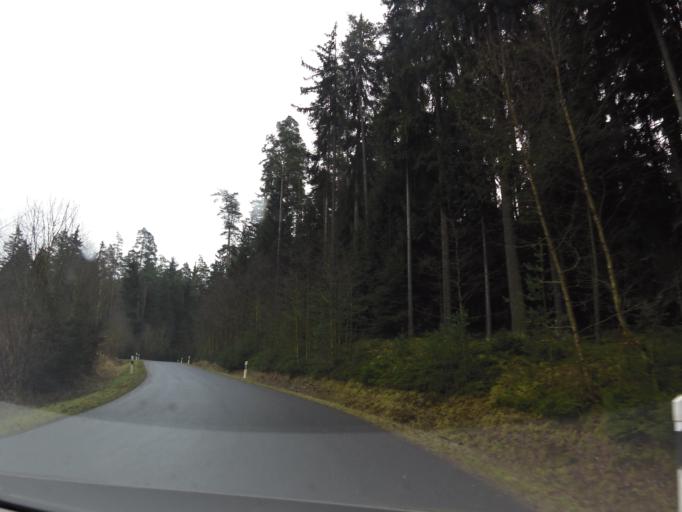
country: DE
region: Bavaria
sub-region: Upper Franconia
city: Wunsiedel
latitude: 50.0614
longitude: 12.0228
